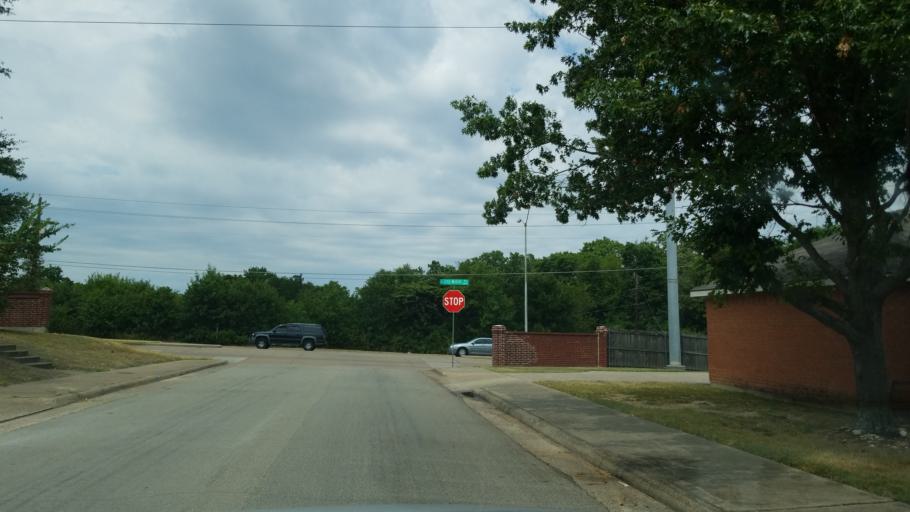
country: US
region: Texas
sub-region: Dallas County
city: Duncanville
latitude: 32.6617
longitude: -96.8536
